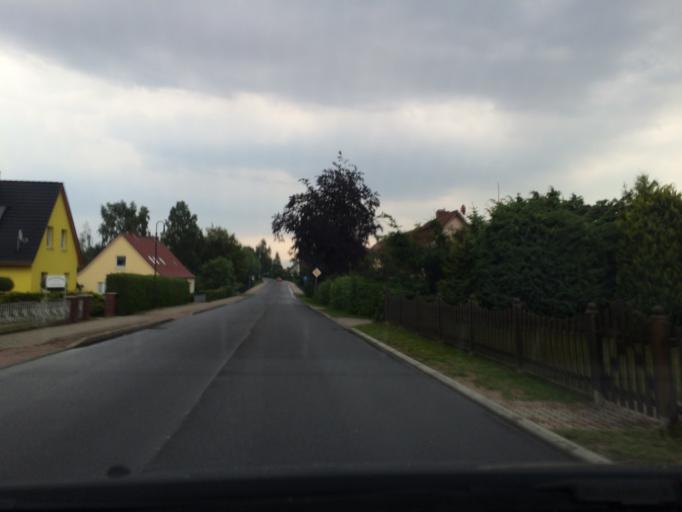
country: DE
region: Mecklenburg-Vorpommern
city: Altenpleen
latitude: 54.3544
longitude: 12.9550
